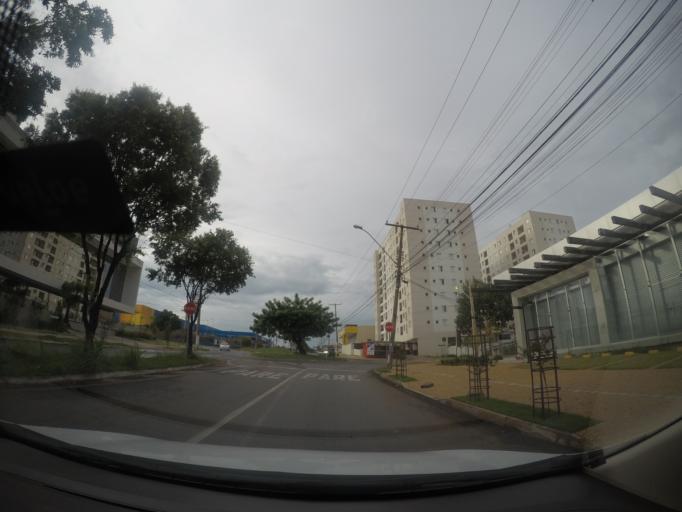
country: BR
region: Goias
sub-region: Goiania
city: Goiania
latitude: -16.7423
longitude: -49.2836
